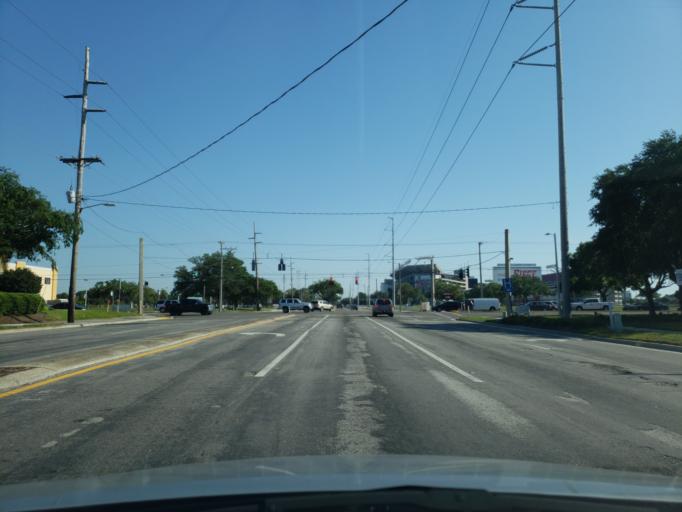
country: US
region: Florida
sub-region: Hillsborough County
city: Egypt Lake-Leto
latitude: 27.9820
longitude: -82.5014
